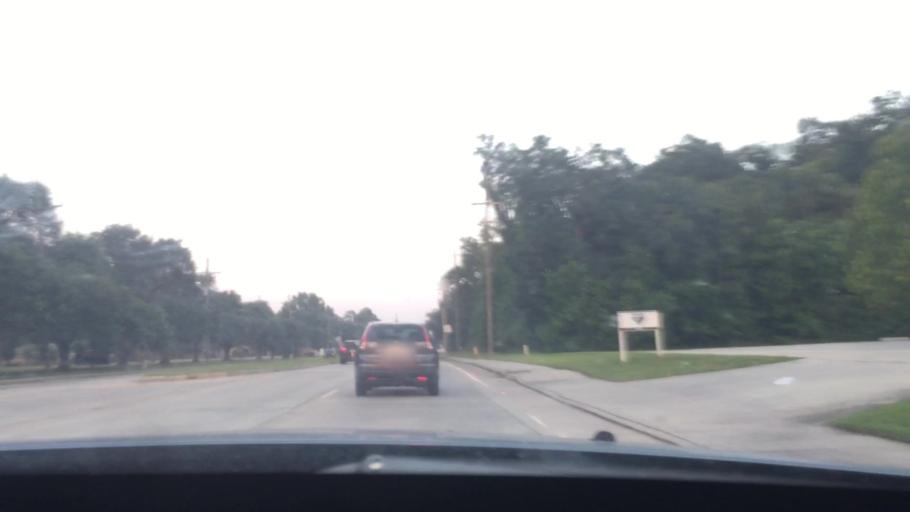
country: US
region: Louisiana
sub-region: East Baton Rouge Parish
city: Shenandoah
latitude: 30.4287
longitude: -91.0209
